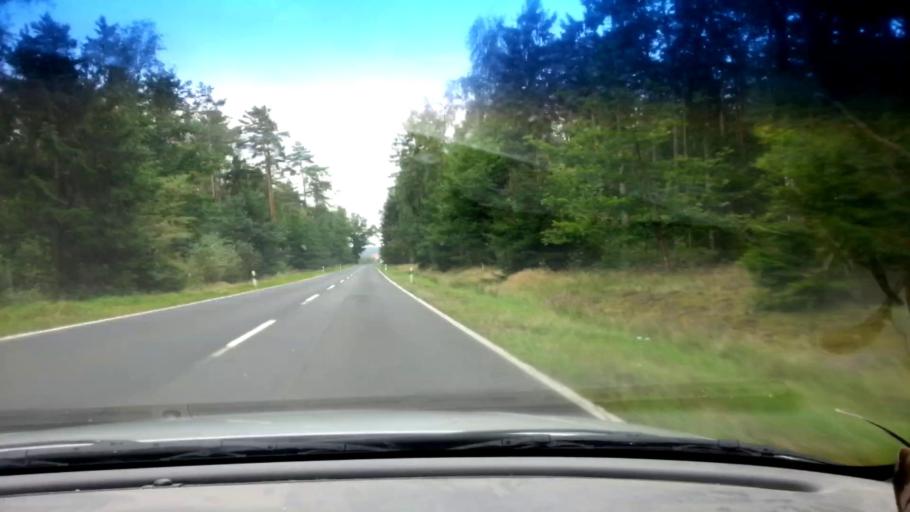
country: DE
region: Bavaria
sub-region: Upper Palatinate
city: Waldsassen
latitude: 50.0181
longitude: 12.3120
